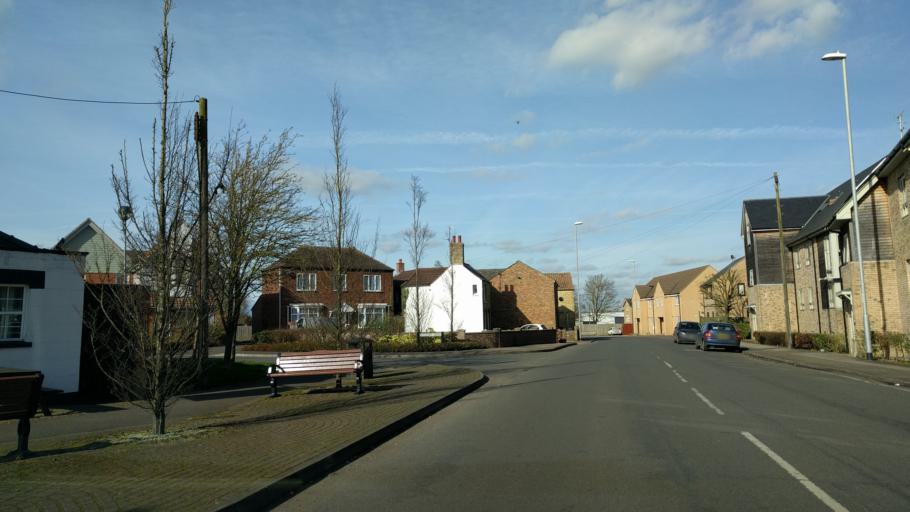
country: GB
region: England
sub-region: Cambridgeshire
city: Chatteris
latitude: 52.4616
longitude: 0.0452
